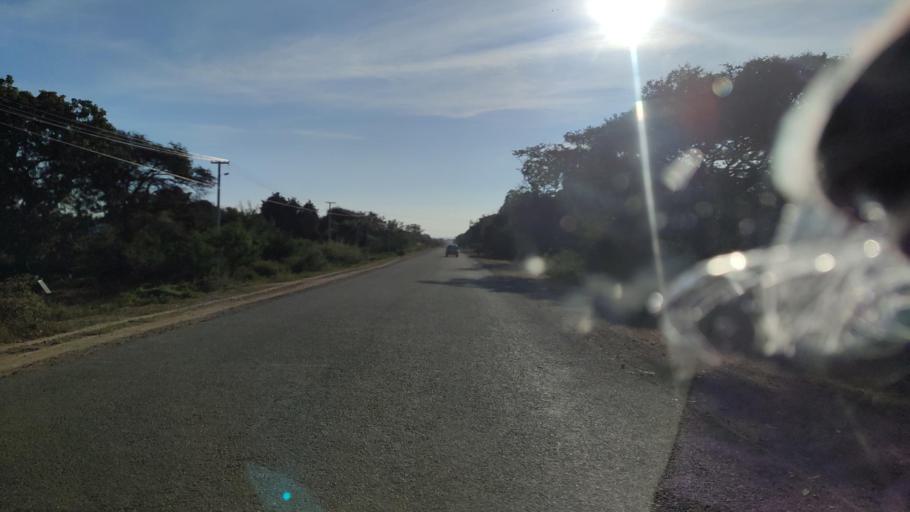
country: MM
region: Mandalay
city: Yamethin
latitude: 20.7258
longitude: 96.1977
